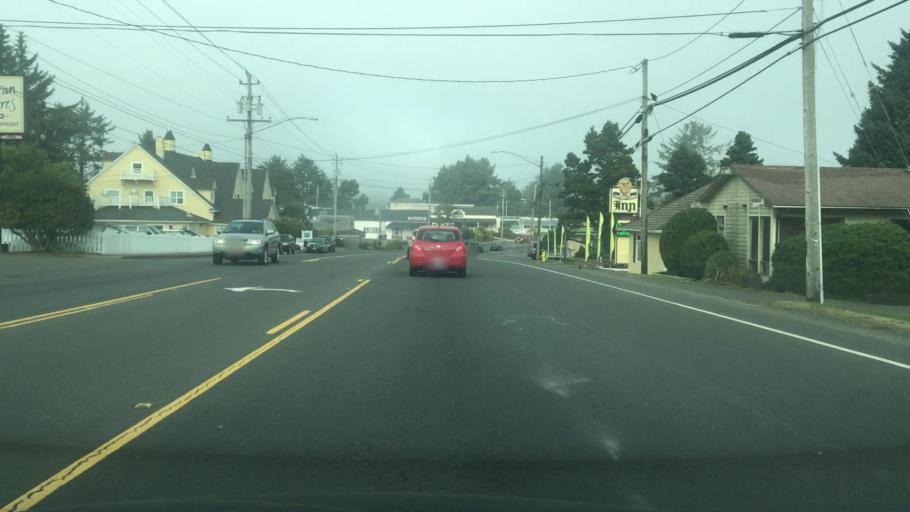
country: US
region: Oregon
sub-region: Lincoln County
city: Lincoln City
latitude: 44.9839
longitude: -124.0072
